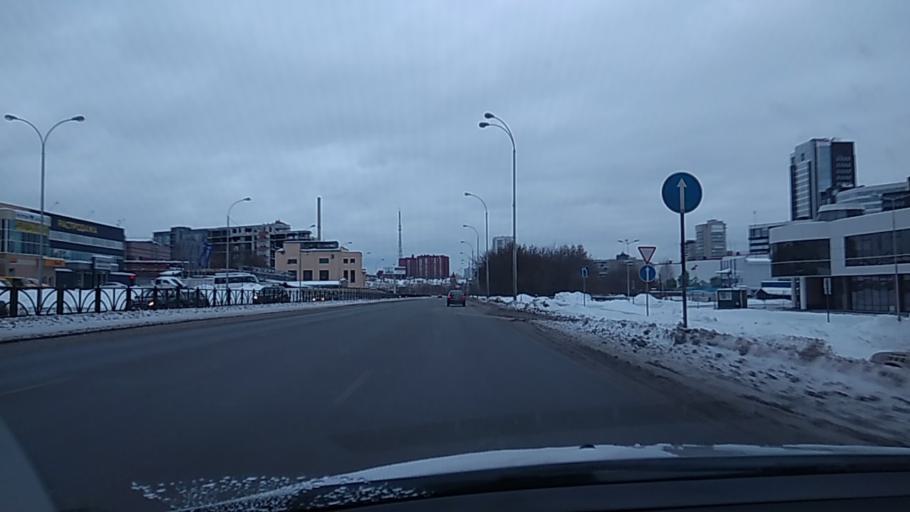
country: RU
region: Sverdlovsk
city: Yekaterinburg
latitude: 56.8129
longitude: 60.6292
